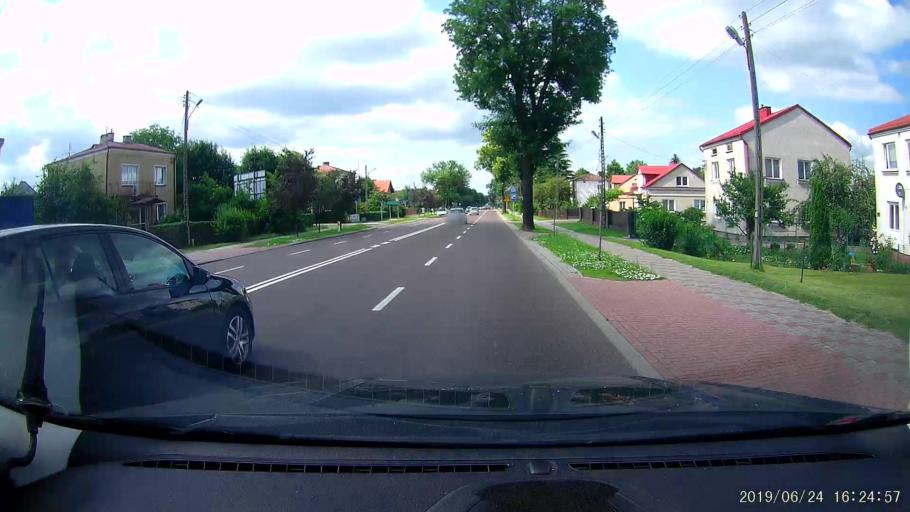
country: PL
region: Lublin Voivodeship
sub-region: Powiat tomaszowski
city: Tomaszow Lubelski
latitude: 50.4399
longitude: 23.4188
